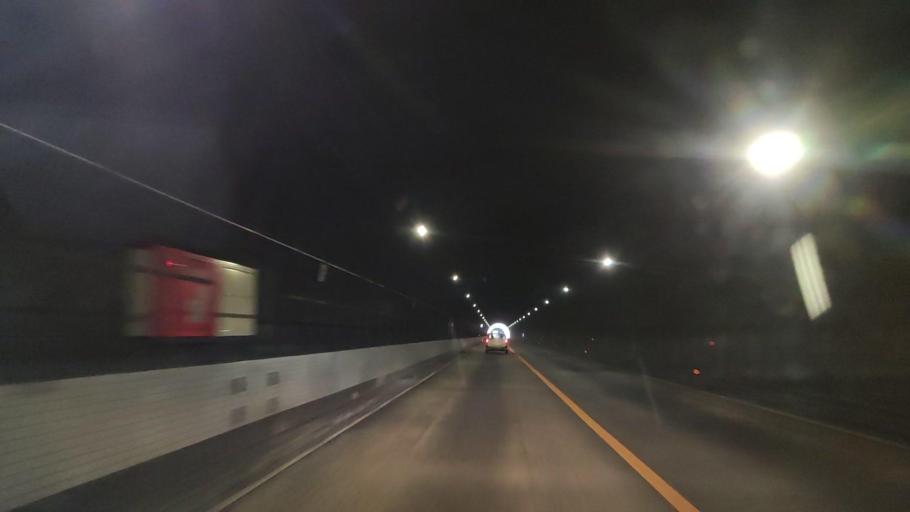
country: JP
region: Okayama
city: Okayama-shi
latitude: 34.7189
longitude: 133.9440
